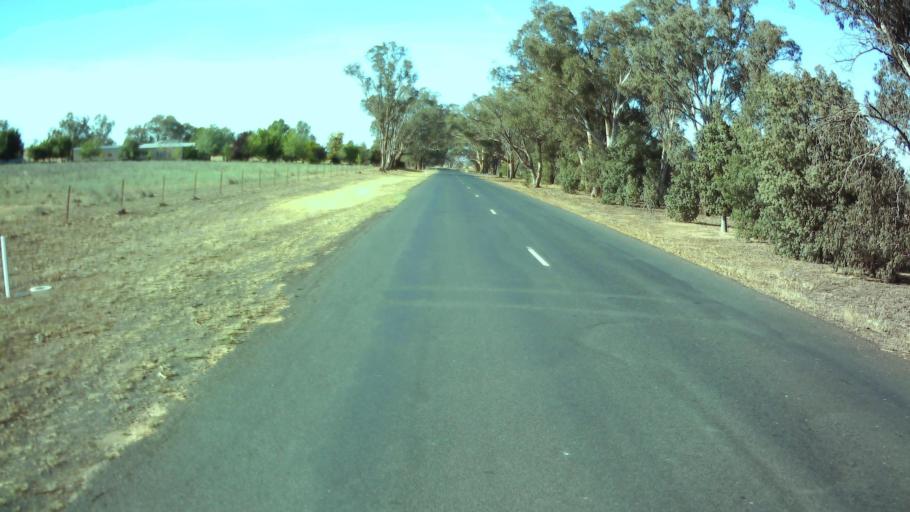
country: AU
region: New South Wales
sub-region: Weddin
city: Grenfell
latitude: -33.9127
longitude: 148.1438
